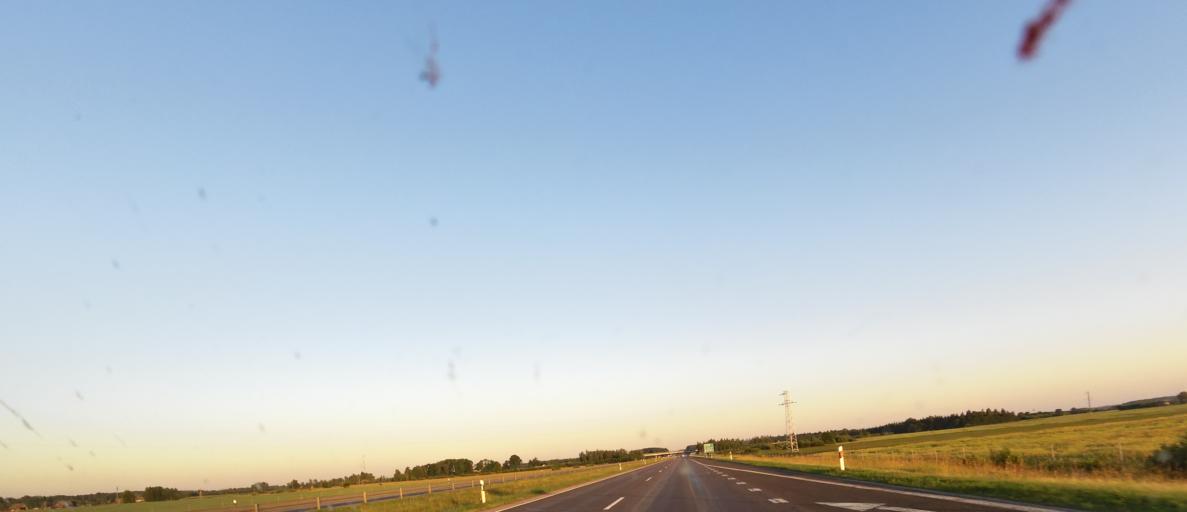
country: LT
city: Sirvintos
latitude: 55.0223
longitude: 24.9070
